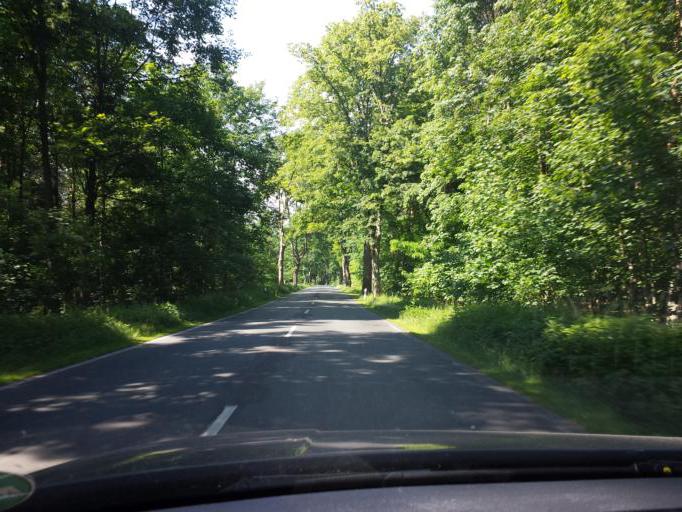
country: DE
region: Brandenburg
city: Ruthnick
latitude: 52.8325
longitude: 13.0142
